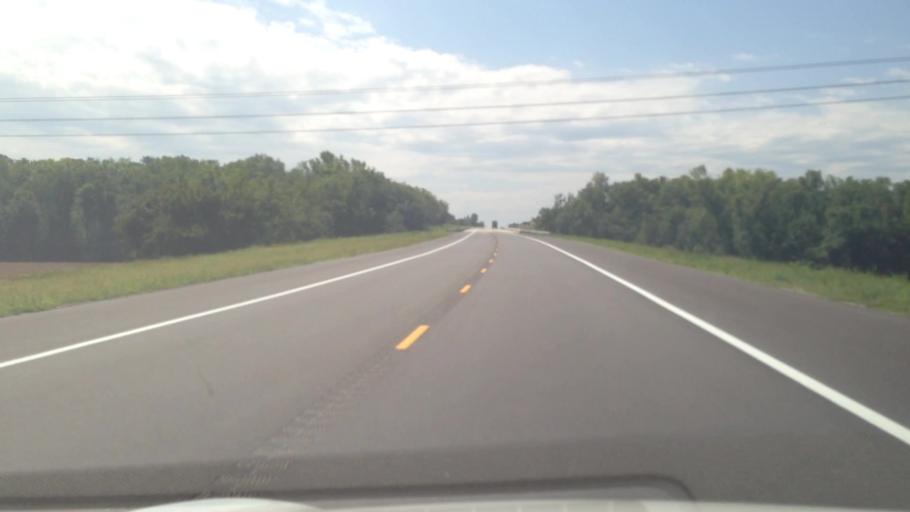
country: US
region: Kansas
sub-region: Anderson County
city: Garnett
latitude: 38.3364
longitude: -95.2490
